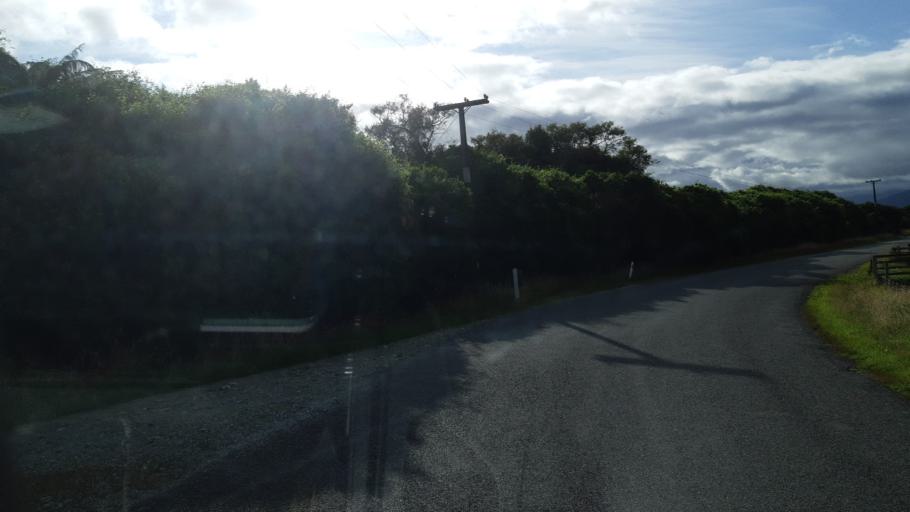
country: NZ
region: West Coast
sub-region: Westland District
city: Hokitika
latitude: -42.7397
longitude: 170.9900
